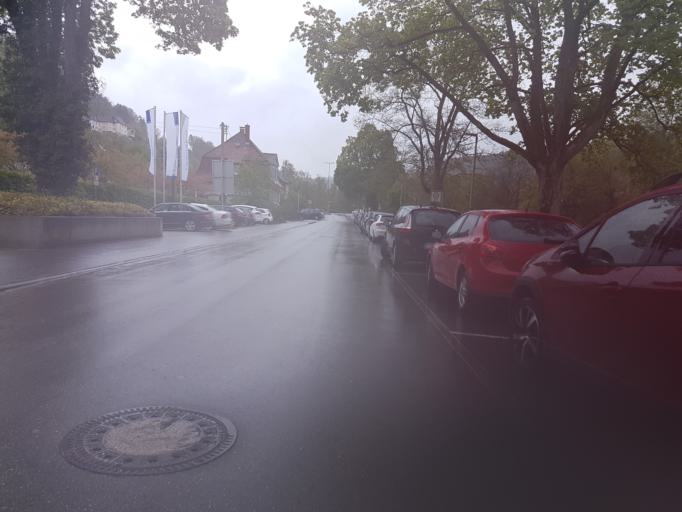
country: DE
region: Baden-Wuerttemberg
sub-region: Freiburg Region
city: Oberndorf
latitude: 48.2959
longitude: 8.5776
